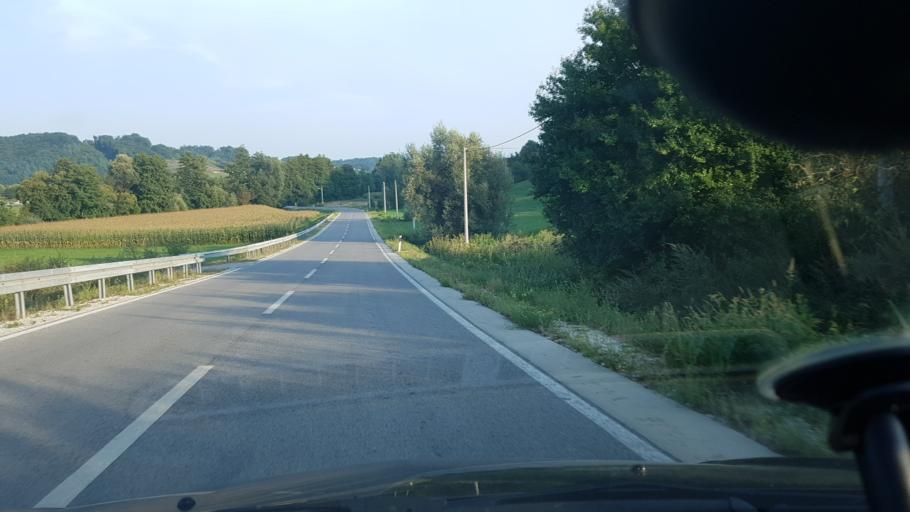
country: HR
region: Krapinsko-Zagorska
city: Pregrada
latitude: 46.1577
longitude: 15.7961
